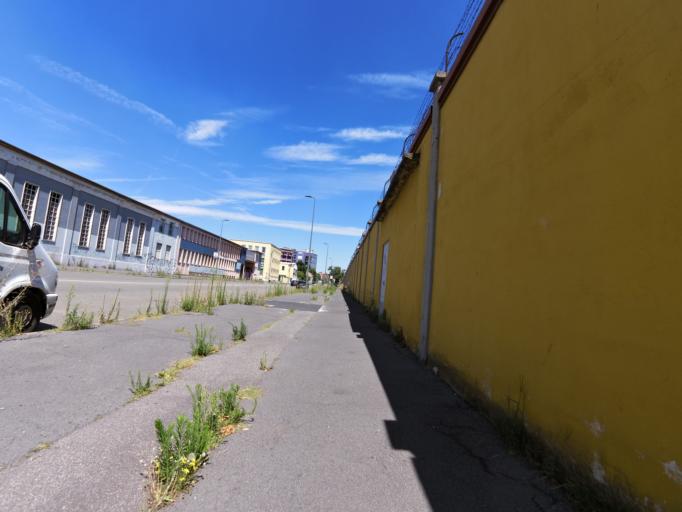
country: IT
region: Lombardy
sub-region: Citta metropolitana di Milano
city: Novegro-Tregarezzo-San Felice
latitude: 45.4743
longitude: 9.2447
